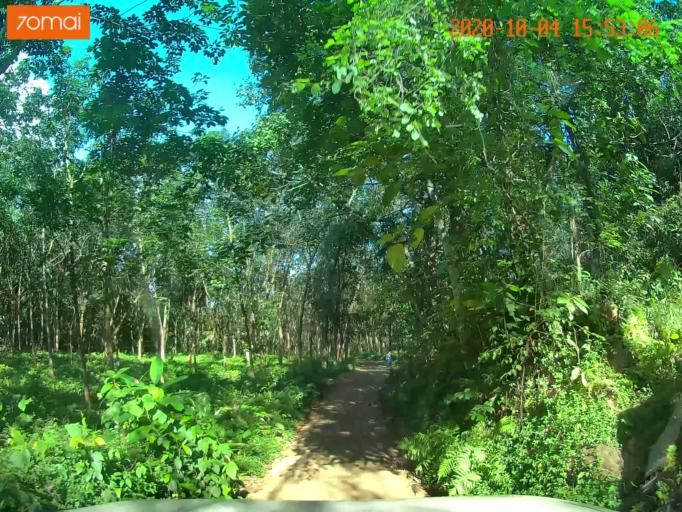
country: IN
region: Kerala
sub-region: Kottayam
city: Palackattumala
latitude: 9.7819
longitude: 76.5554
